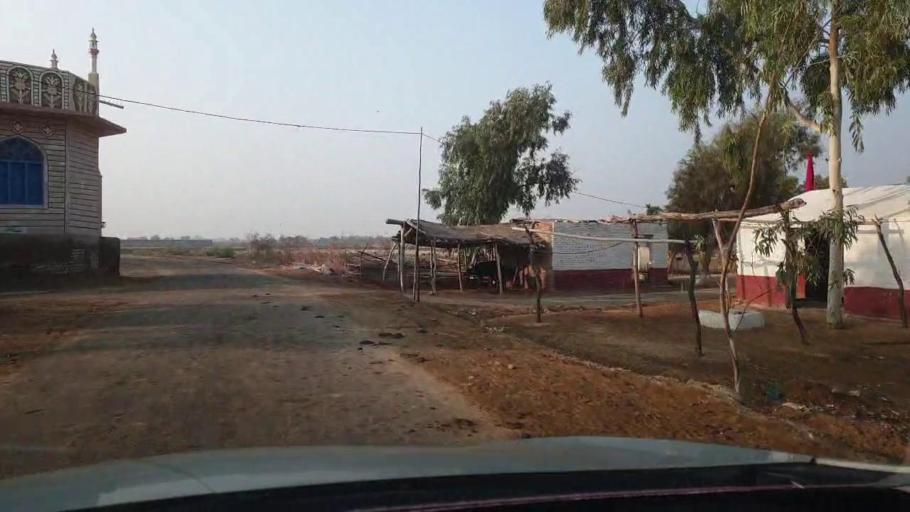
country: PK
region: Sindh
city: Sehwan
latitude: 26.3538
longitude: 67.7615
